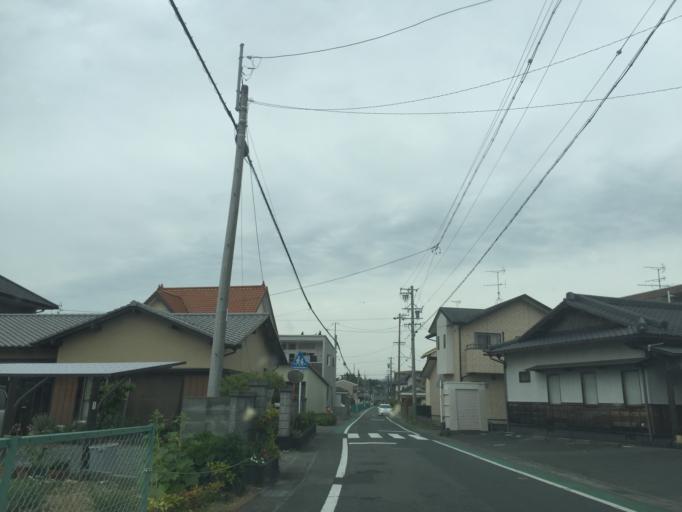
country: JP
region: Shizuoka
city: Kakegawa
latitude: 34.7765
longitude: 137.9960
